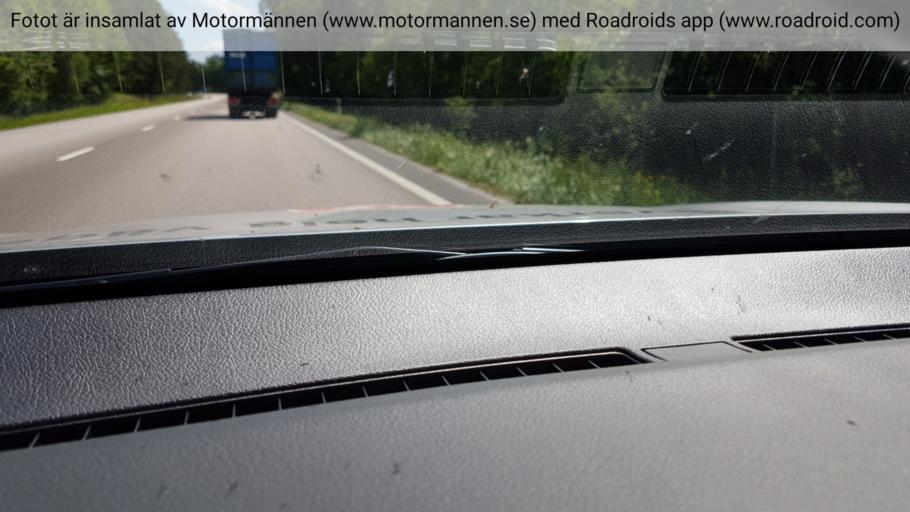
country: SE
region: Vaestra Goetaland
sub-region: Lidkopings Kommun
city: Vinninga
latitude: 58.4230
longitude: 13.3402
